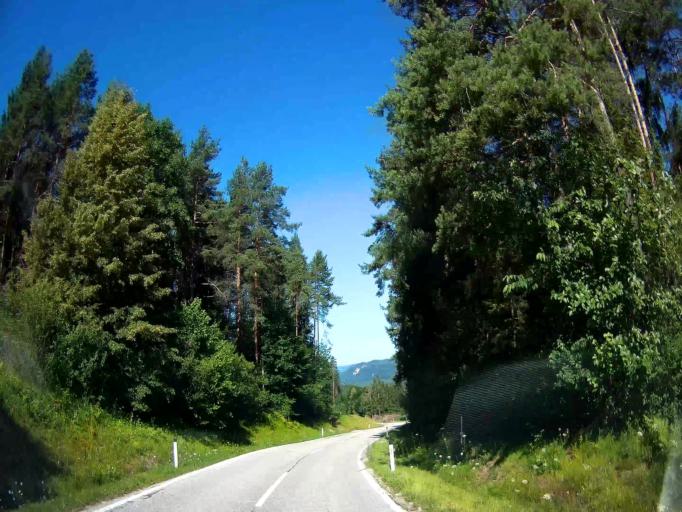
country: AT
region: Carinthia
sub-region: Politischer Bezirk Klagenfurt Land
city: Ebenthal
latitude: 46.5383
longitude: 14.3906
